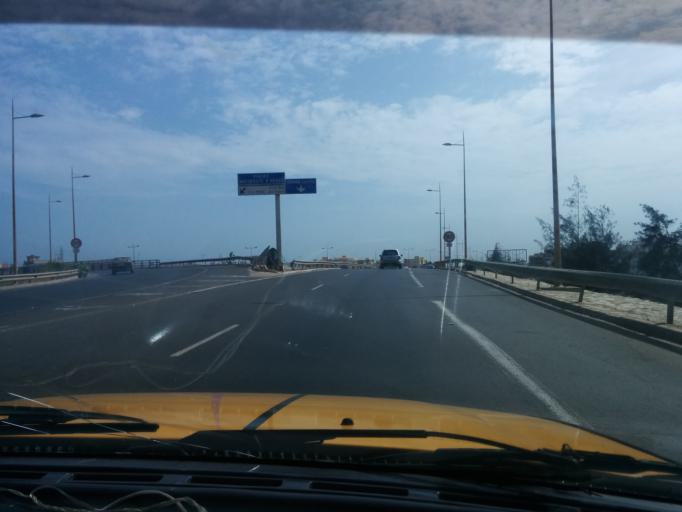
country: SN
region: Dakar
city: Grand Dakar
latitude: 14.7404
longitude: -17.4398
